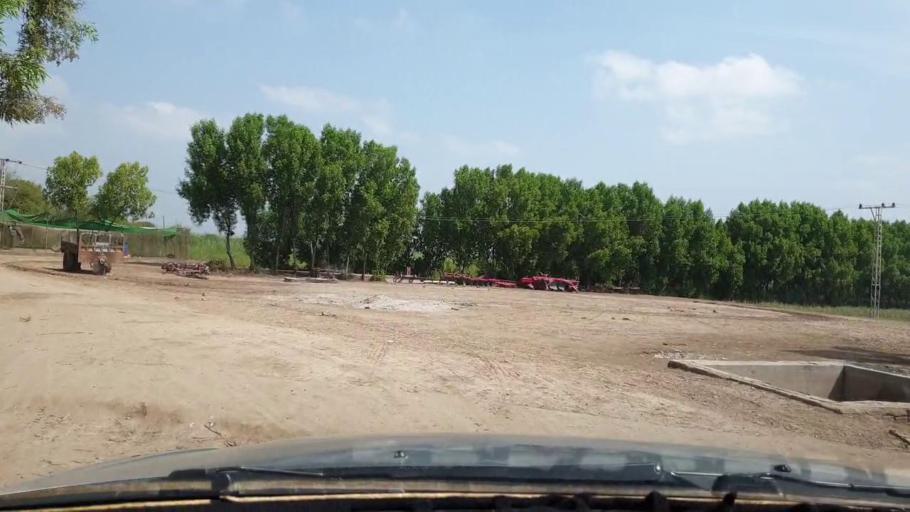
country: PK
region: Sindh
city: Matli
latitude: 25.0949
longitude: 68.6931
